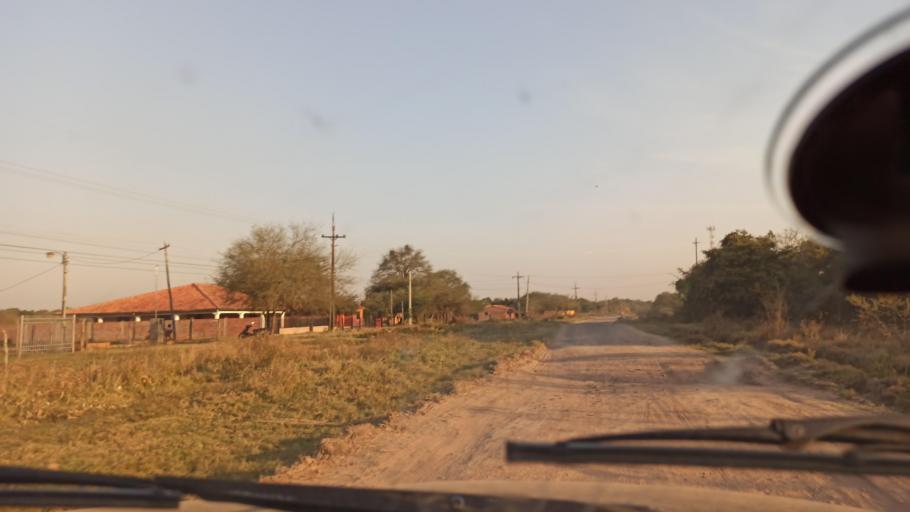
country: PY
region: Presidente Hayes
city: Nanawa
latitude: -25.2292
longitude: -57.6305
